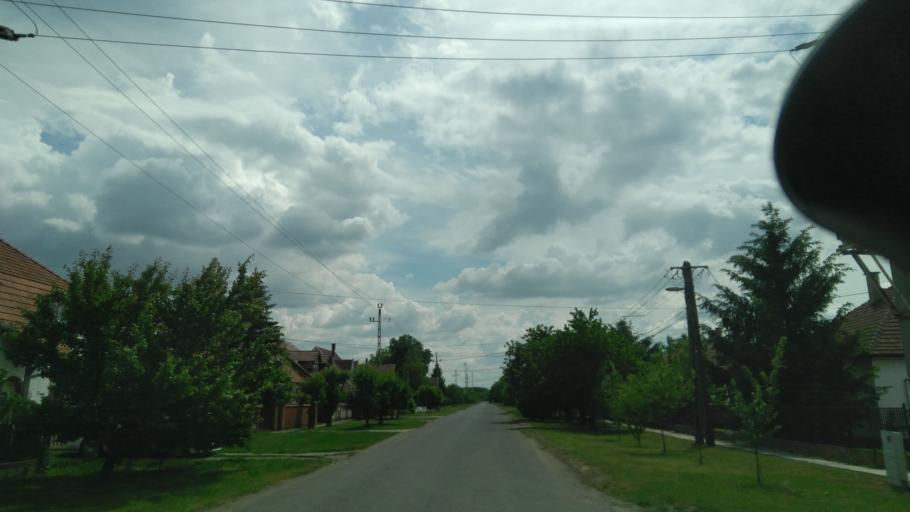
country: HU
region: Bekes
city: Mezohegyes
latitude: 46.3192
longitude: 20.8077
